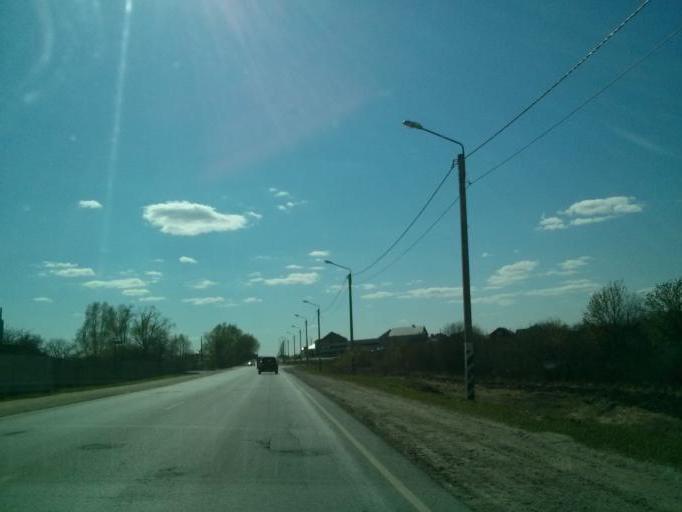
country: RU
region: Nizjnij Novgorod
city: Pavlovo
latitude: 55.9474
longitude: 43.1088
